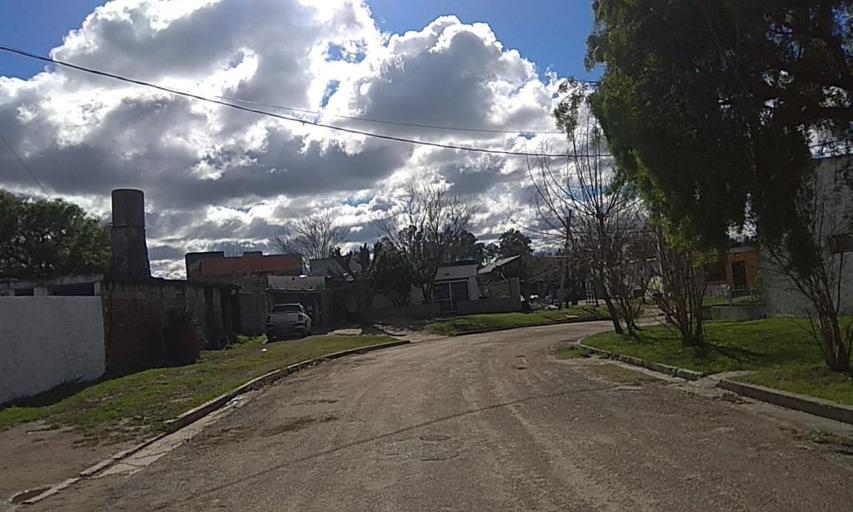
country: UY
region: Florida
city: Florida
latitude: -34.0923
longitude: -56.2262
